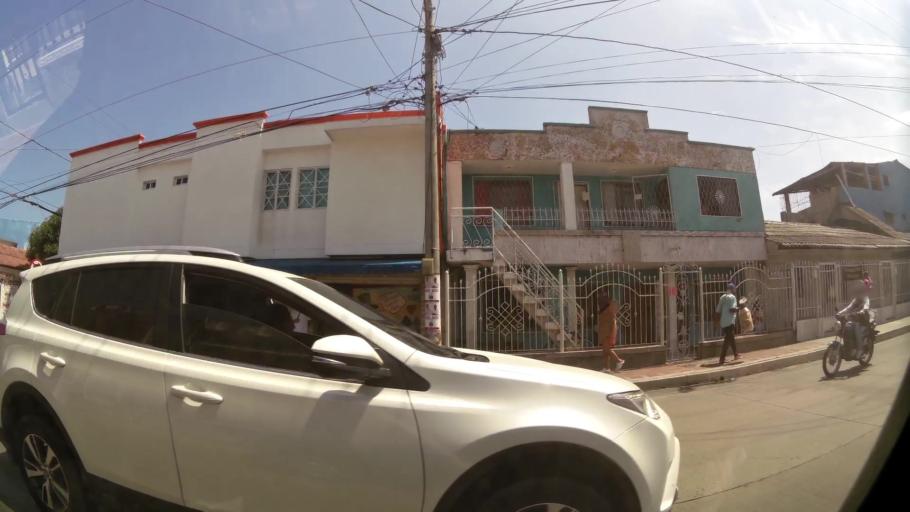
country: CO
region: Atlantico
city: Barranquilla
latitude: 10.9711
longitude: -74.8109
